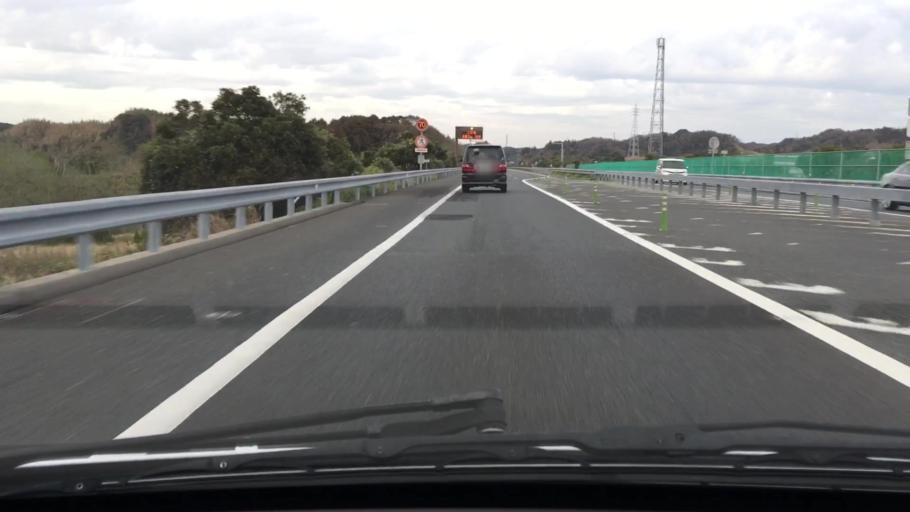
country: JP
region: Chiba
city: Kimitsu
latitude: 35.2448
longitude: 139.8896
